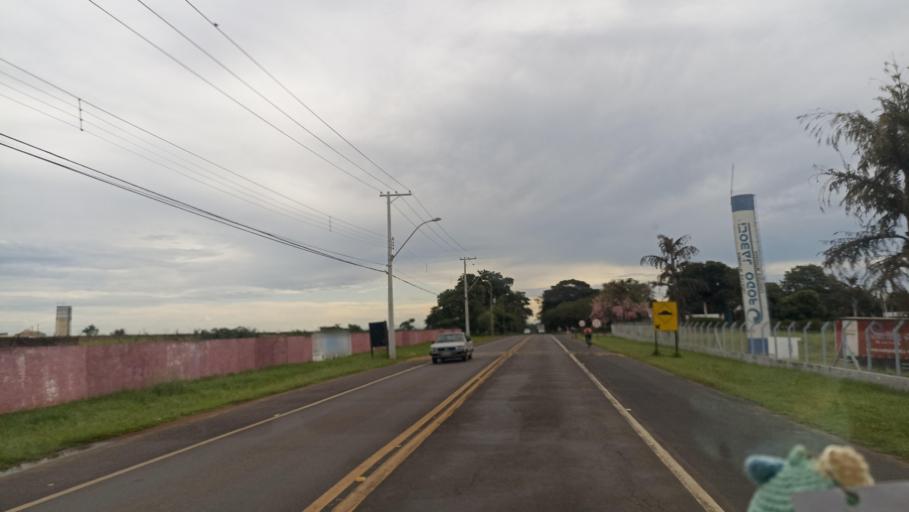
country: BR
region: Sao Paulo
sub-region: Jaboticabal
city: Jaboticabal
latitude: -21.2607
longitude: -48.3325
